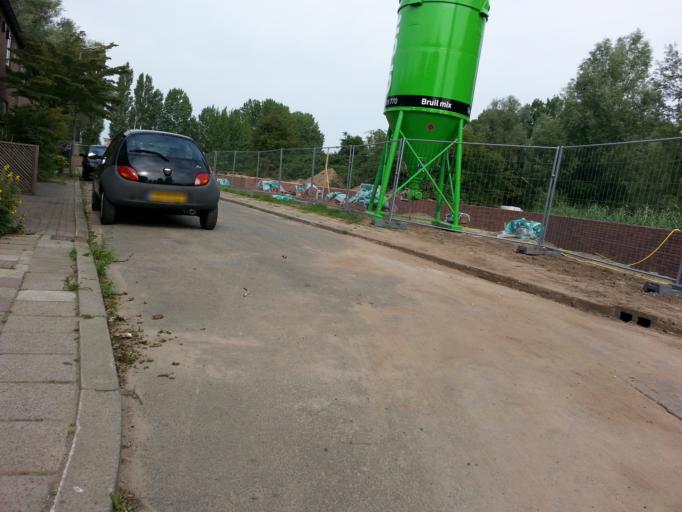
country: NL
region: Utrecht
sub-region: Gemeente Amersfoort
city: Amersfoort
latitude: 52.1646
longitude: 5.3781
